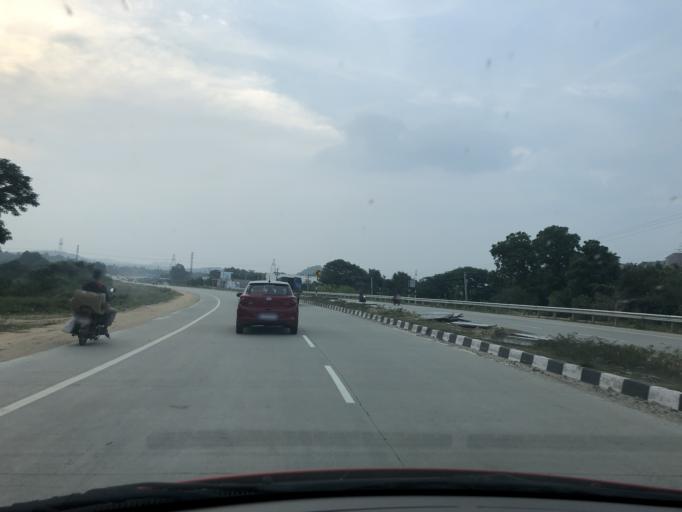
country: IN
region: Andhra Pradesh
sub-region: Chittoor
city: Chittoor
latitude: 13.1978
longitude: 78.9983
